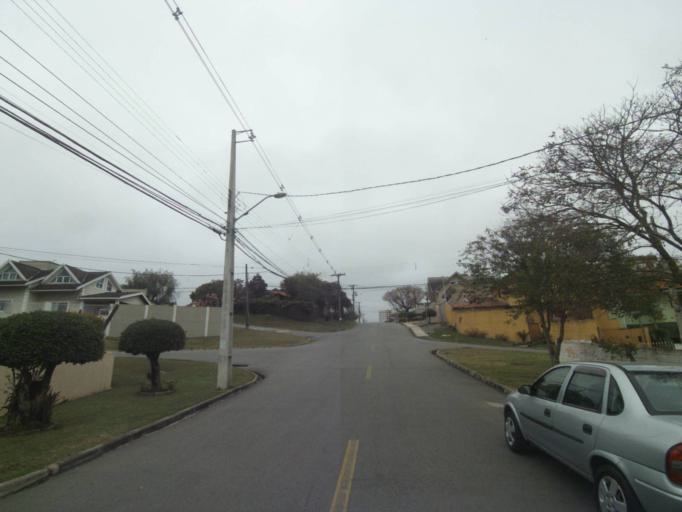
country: BR
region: Parana
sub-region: Curitiba
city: Curitiba
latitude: -25.5009
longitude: -49.2923
